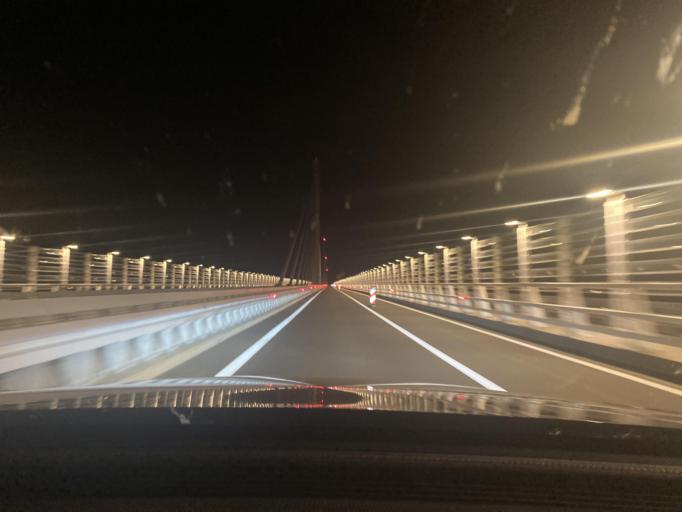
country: BA
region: Federation of Bosnia and Herzegovina
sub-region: Hercegovacko-Bosanski Kanton
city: Neum
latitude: 42.9382
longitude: 17.5422
